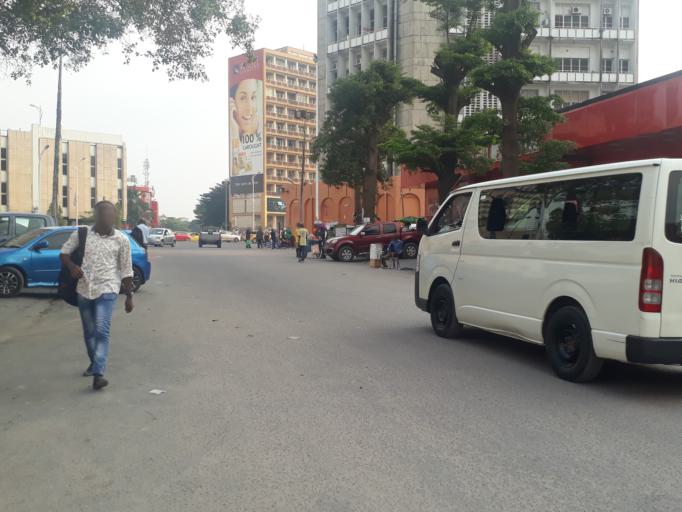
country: CD
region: Kinshasa
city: Kinshasa
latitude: -4.3025
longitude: 15.3103
